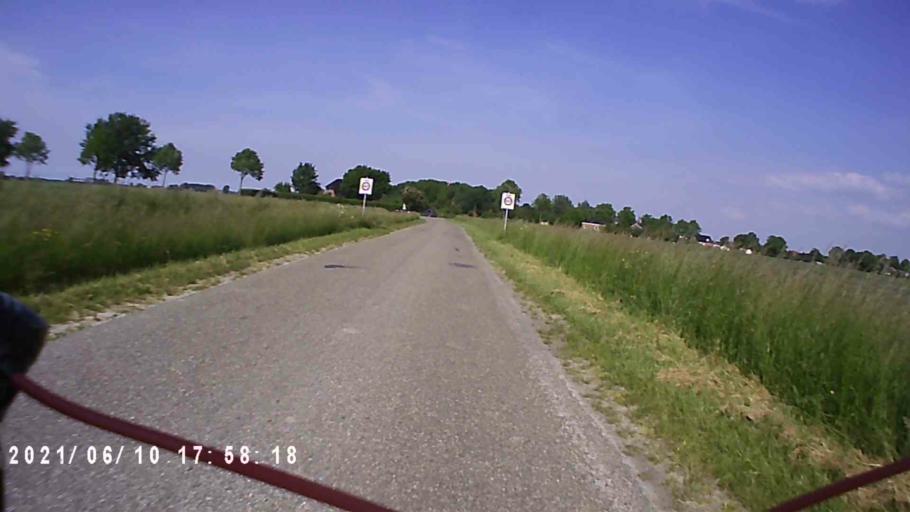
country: NL
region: Groningen
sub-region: Gemeente De Marne
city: Ulrum
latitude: 53.3348
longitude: 6.3340
